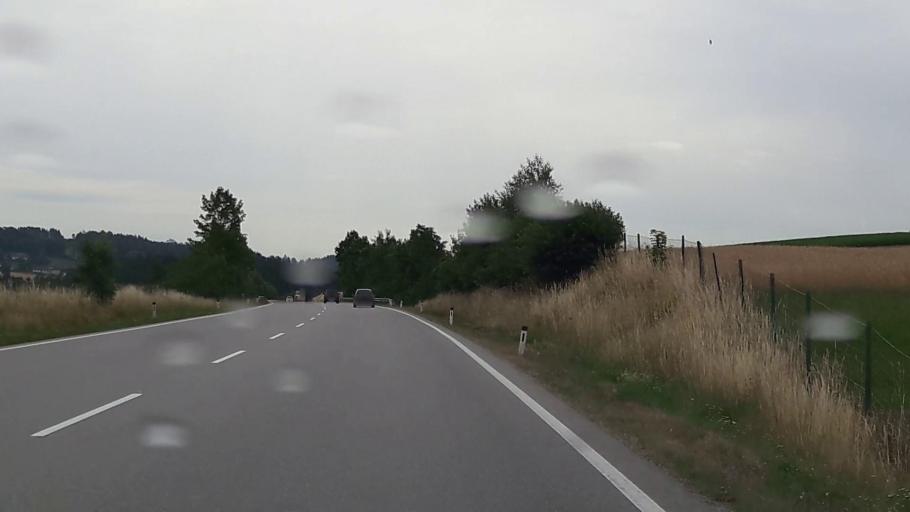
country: AT
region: Upper Austria
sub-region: Politischer Bezirk Rohrbach
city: Kleinzell im Muehlkreis
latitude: 48.4704
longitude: 14.0083
